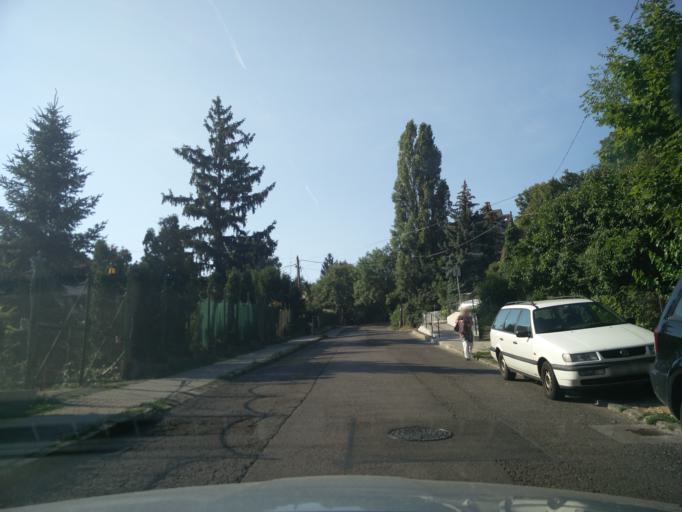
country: HU
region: Budapest
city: Budapest XII. keruelet
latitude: 47.5126
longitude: 18.9898
